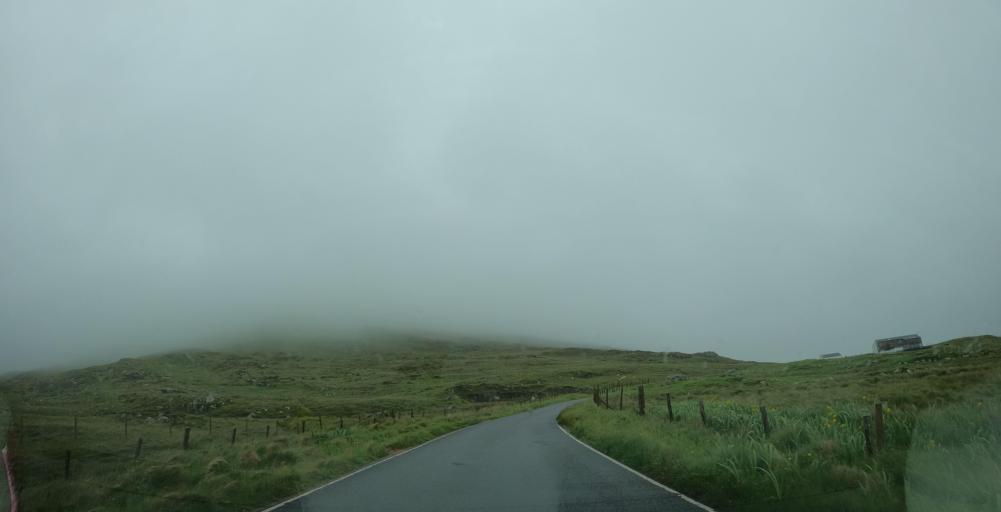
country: GB
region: Scotland
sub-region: Eilean Siar
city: Barra
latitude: 56.9598
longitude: -7.4697
